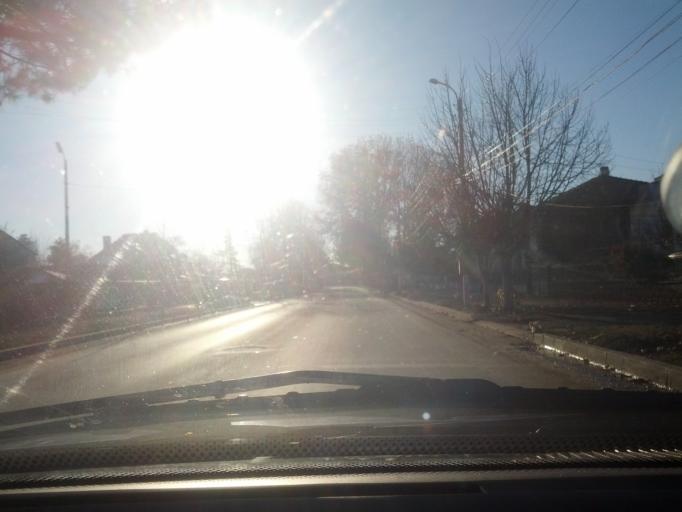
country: BG
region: Vratsa
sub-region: Obshtina Miziya
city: Miziya
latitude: 43.6876
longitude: 23.8050
